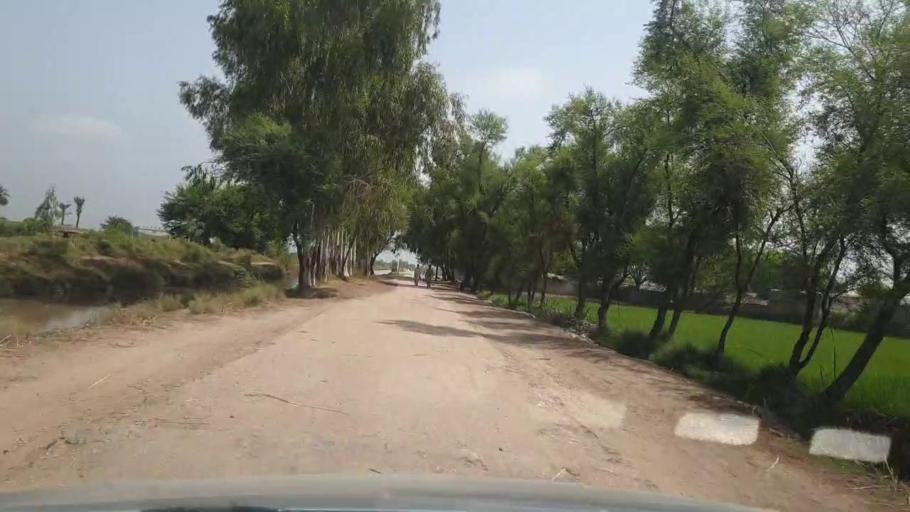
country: PK
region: Sindh
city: Ratodero
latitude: 27.9253
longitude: 68.3584
